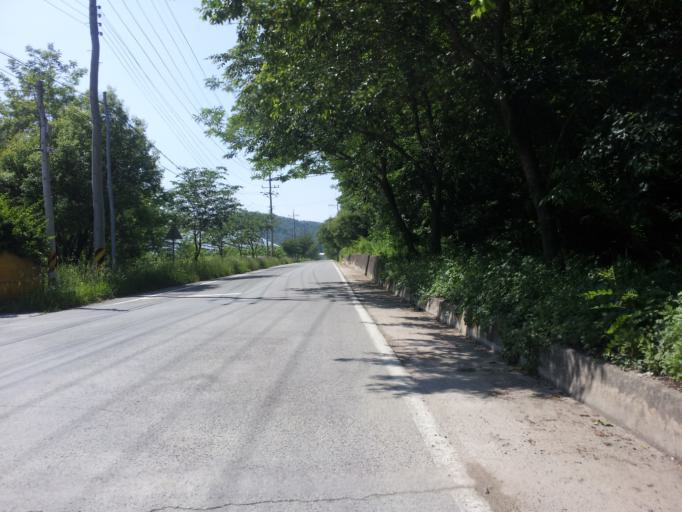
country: KR
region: Chungcheongbuk-do
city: Okcheon
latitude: 36.4526
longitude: 127.6772
